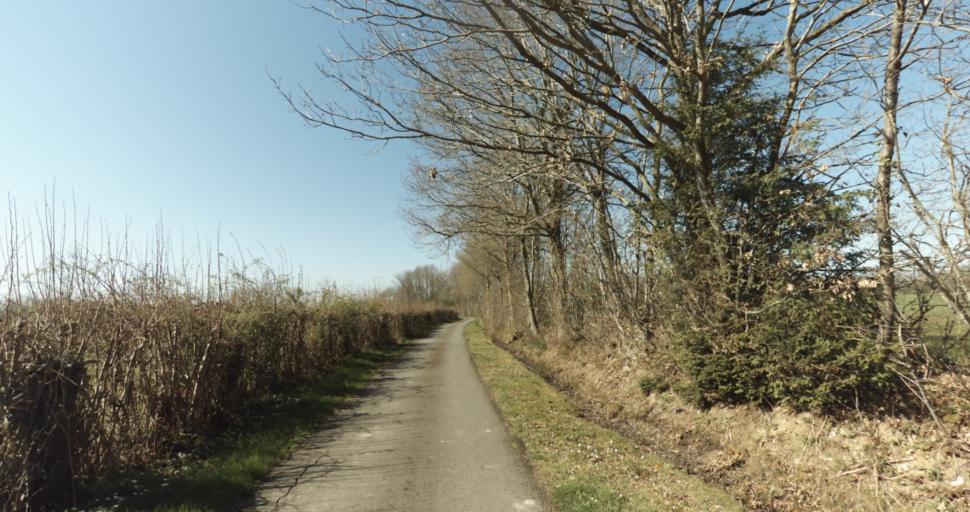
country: FR
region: Lower Normandy
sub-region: Departement du Calvados
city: Livarot
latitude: 49.0242
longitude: 0.1063
